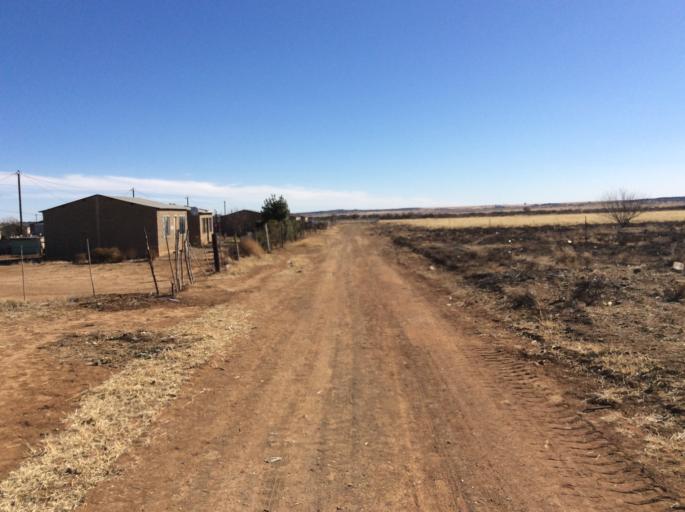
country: ZA
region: Orange Free State
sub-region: Lejweleputswa District Municipality
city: Brandfort
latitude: -28.7303
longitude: 26.1074
